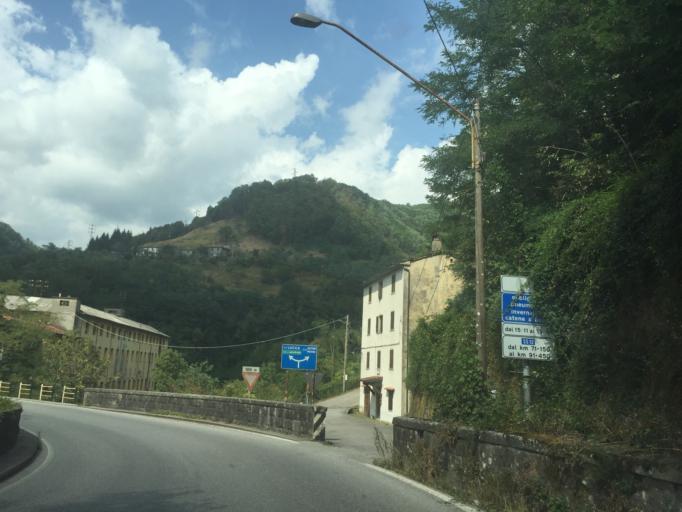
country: IT
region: Tuscany
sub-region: Provincia di Pistoia
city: San Marcello Pistoiese
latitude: 44.0635
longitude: 10.7673
